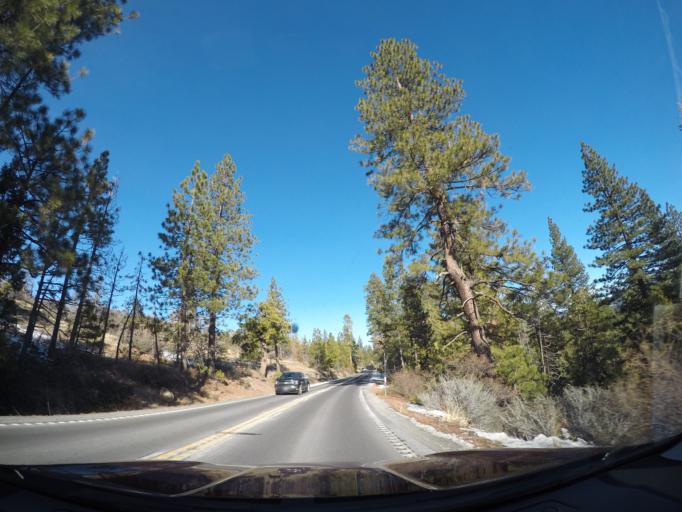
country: US
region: California
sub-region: Tuolumne County
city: Twain Harte
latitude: 38.1454
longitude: -120.0841
